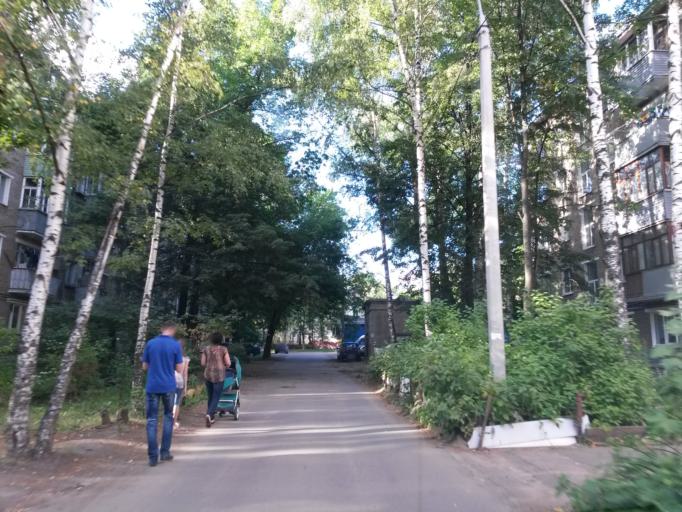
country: RU
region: Jaroslavl
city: Yaroslavl
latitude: 57.5788
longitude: 39.8405
